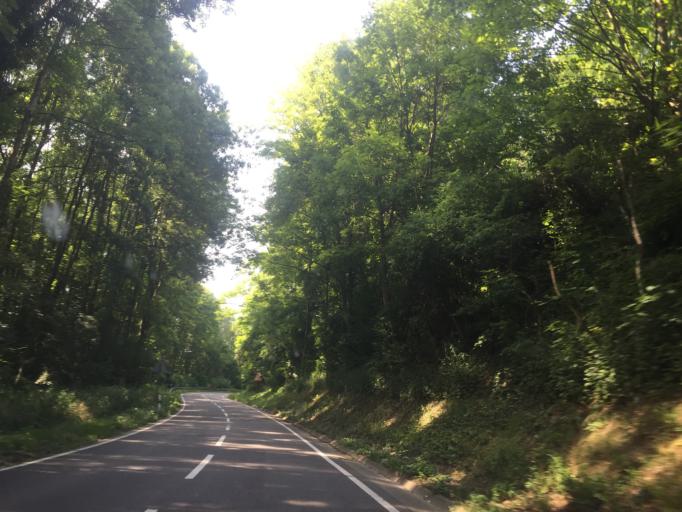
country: DE
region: Baden-Wuerttemberg
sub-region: Karlsruhe Region
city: Horrenberg
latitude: 49.2881
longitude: 8.7628
